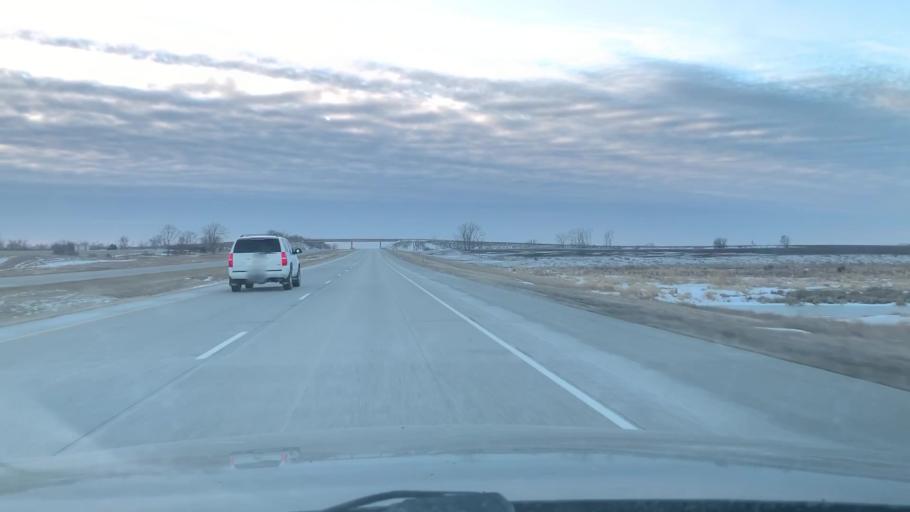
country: US
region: North Dakota
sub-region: Ransom County
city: Sheldon
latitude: 46.8762
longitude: -97.5902
